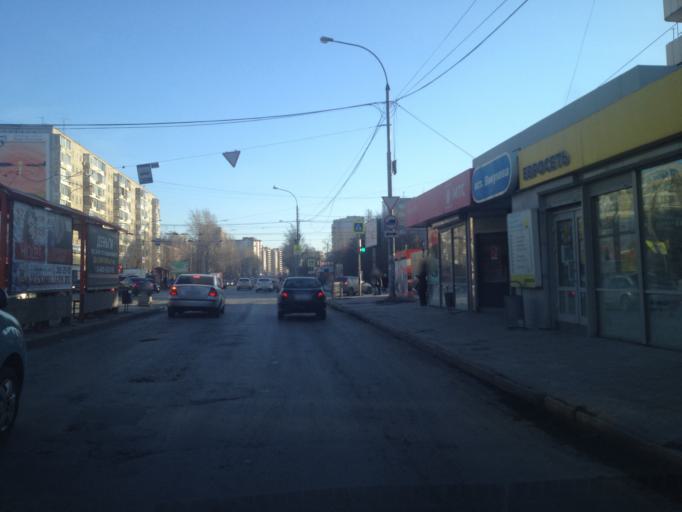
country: RU
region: Sverdlovsk
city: Sovkhoznyy
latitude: 56.8317
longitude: 60.5448
